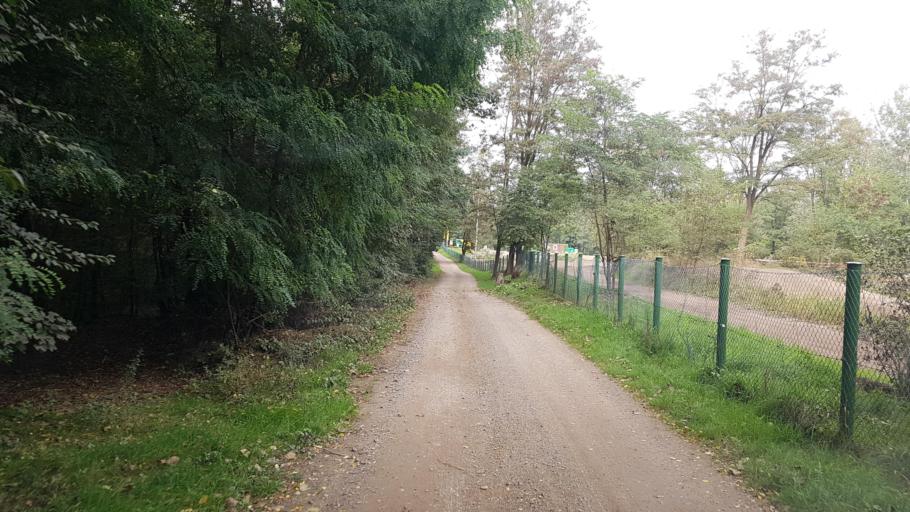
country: DE
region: Brandenburg
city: Lauchhammer
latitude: 51.5049
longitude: 13.7709
